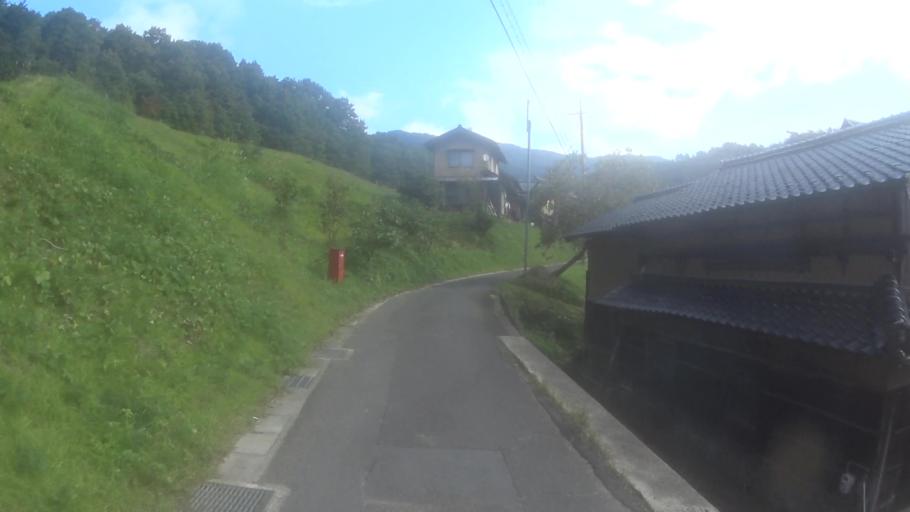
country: JP
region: Kyoto
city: Miyazu
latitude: 35.6123
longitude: 135.1494
